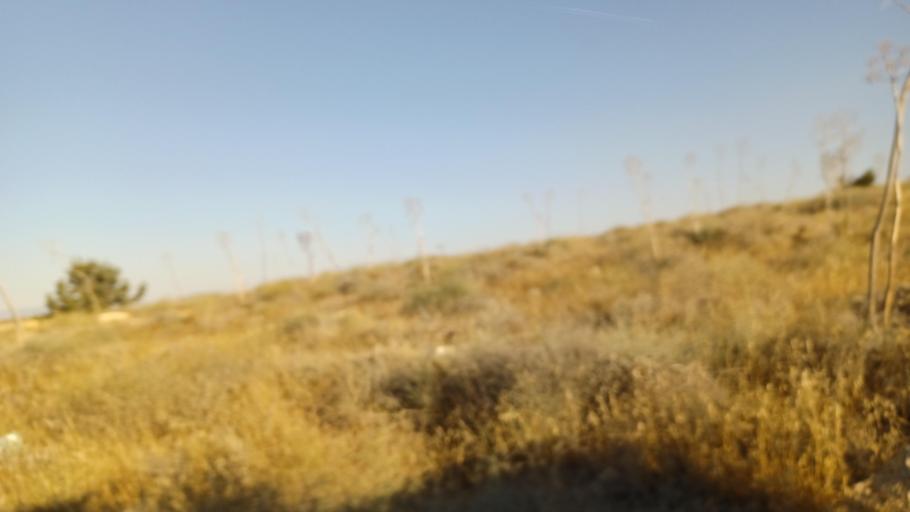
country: CY
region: Larnaka
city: Pyla
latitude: 34.9900
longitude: 33.7072
